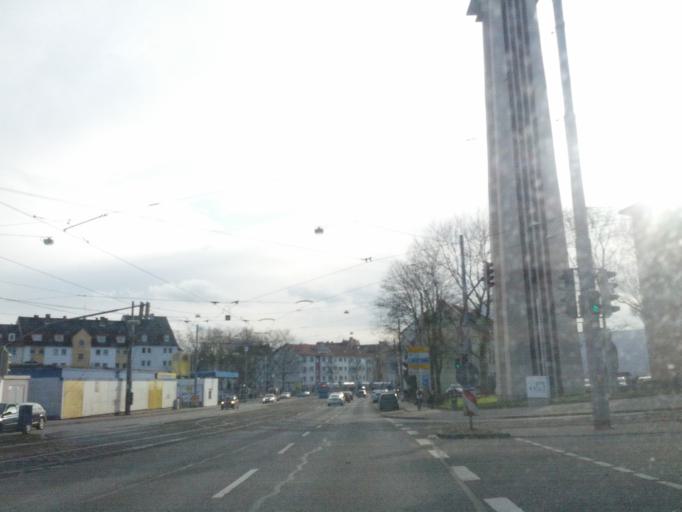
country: DE
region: Hesse
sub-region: Regierungsbezirk Kassel
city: Kassel
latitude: 51.3248
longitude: 9.5130
